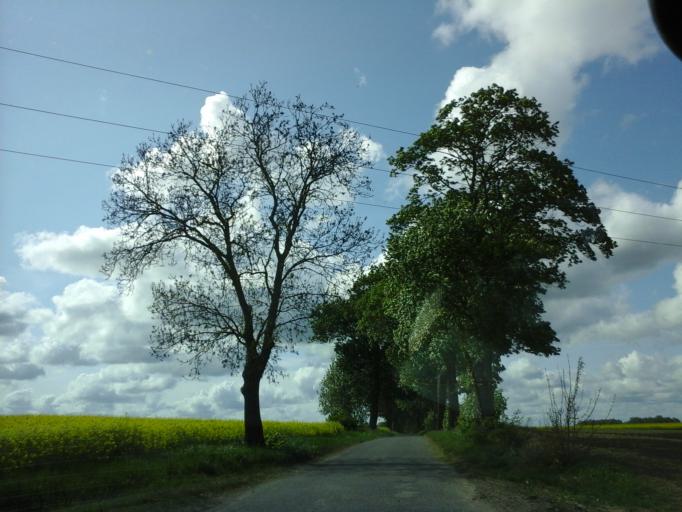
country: PL
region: West Pomeranian Voivodeship
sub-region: Powiat choszczenski
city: Choszczno
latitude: 53.1331
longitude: 15.3673
